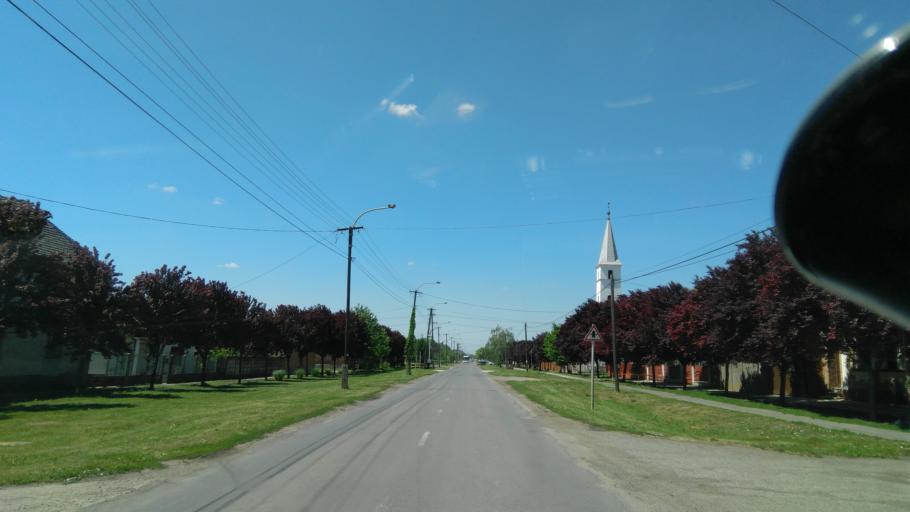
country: HU
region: Bekes
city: Kunagota
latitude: 46.4261
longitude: 21.0535
